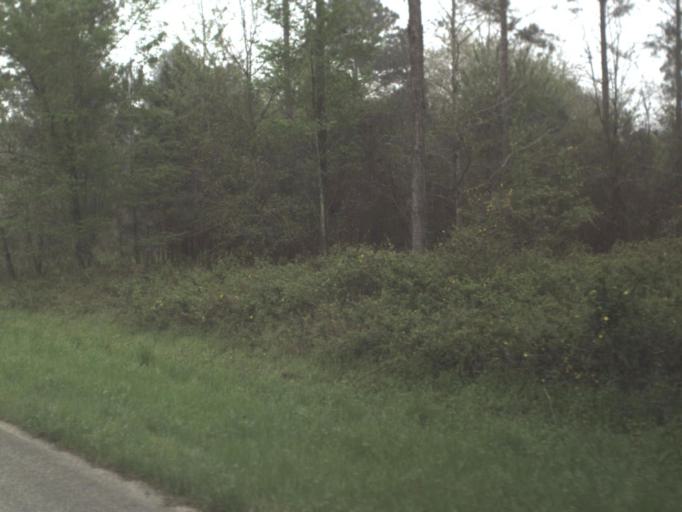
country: US
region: Florida
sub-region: Gadsden County
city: Gretna
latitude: 30.5297
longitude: -84.6870
